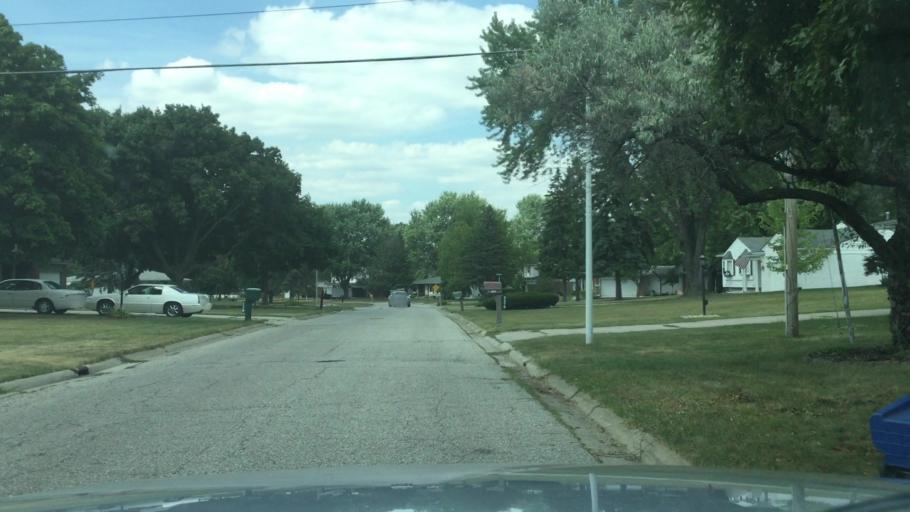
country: US
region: Michigan
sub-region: Genesee County
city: Grand Blanc
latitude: 42.9479
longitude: -83.6723
